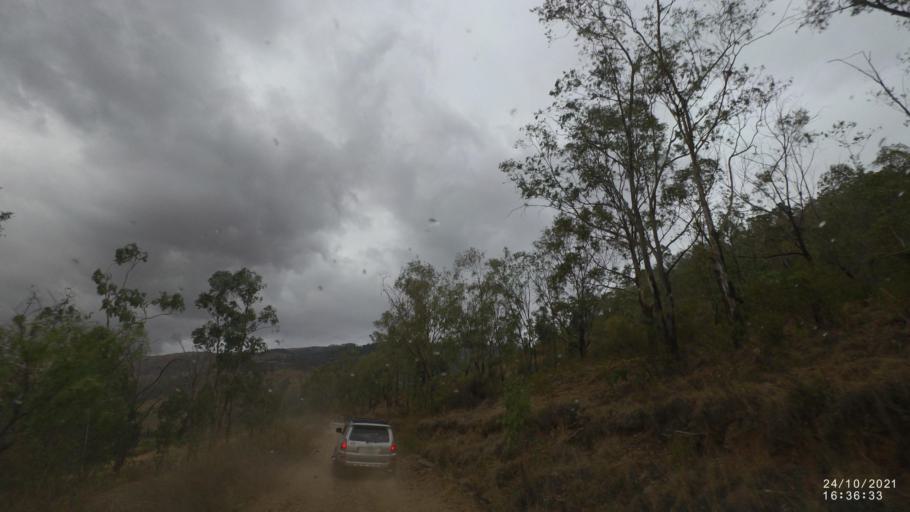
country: BO
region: Cochabamba
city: Cochabamba
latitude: -17.3438
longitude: -66.1495
